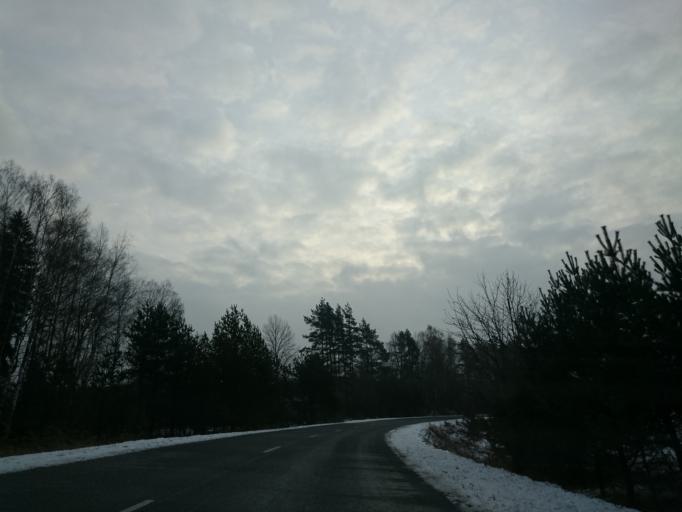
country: LV
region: Seja
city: Loja
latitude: 57.1882
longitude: 24.6014
